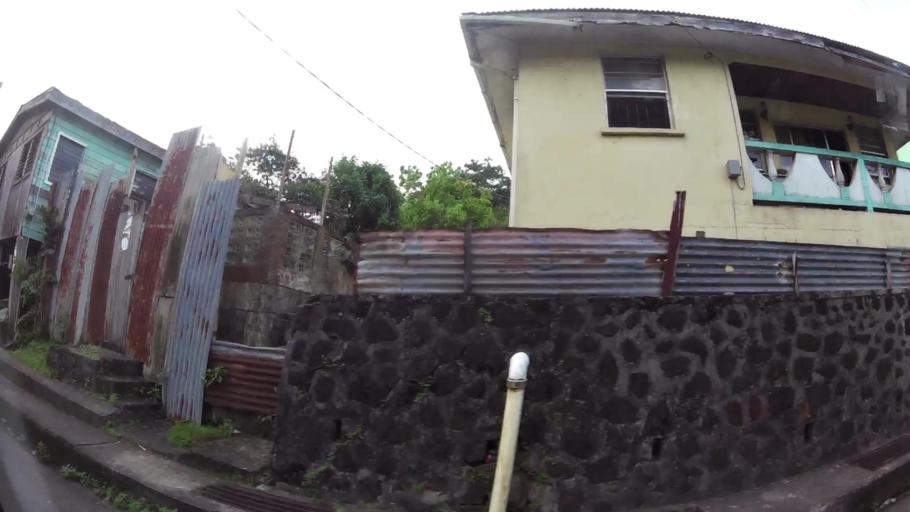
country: LC
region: Castries Quarter
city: Bisee
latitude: 14.0027
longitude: -60.9836
